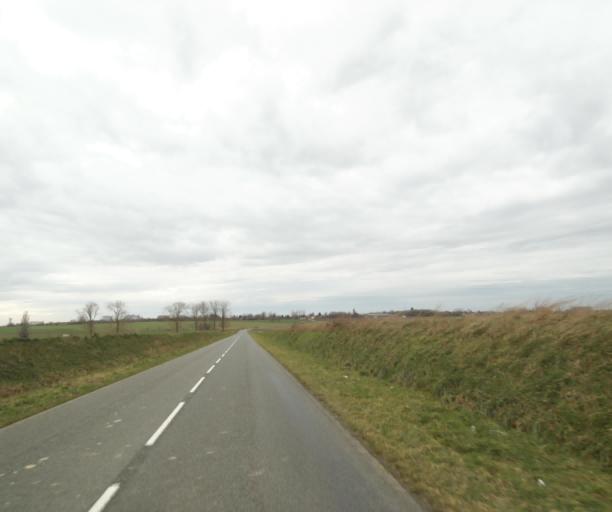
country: FR
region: Nord-Pas-de-Calais
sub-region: Departement du Nord
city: Curgies
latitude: 50.3331
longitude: 3.6236
